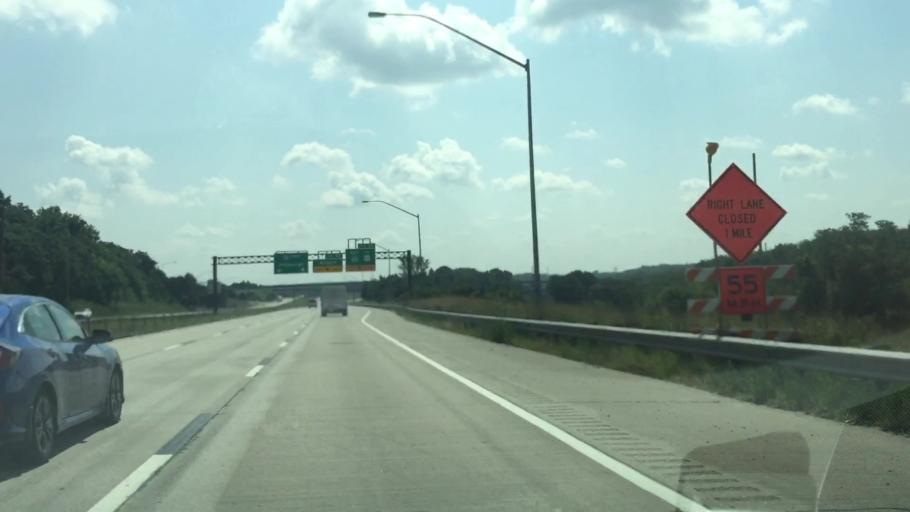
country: US
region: Pennsylvania
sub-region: Allegheny County
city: Imperial
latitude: 40.4954
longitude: -80.2786
